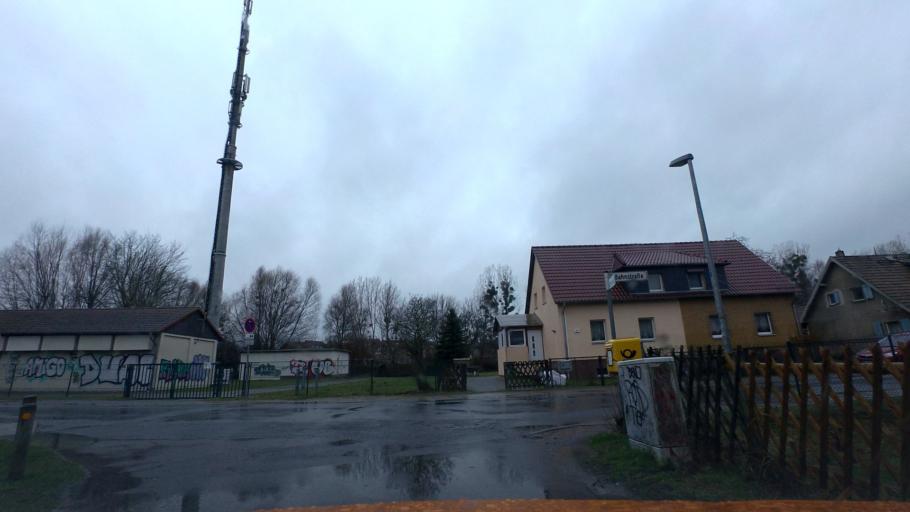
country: DE
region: Brandenburg
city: Brieselang
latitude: 52.5841
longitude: 13.0006
